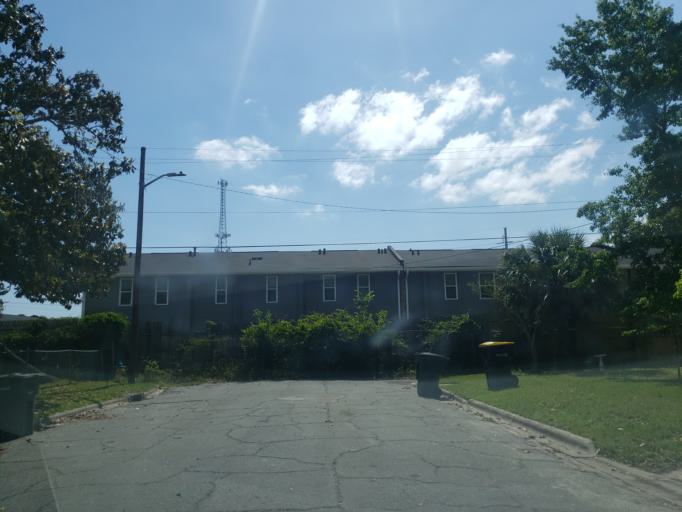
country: US
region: Georgia
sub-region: Chatham County
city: Thunderbolt
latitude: 32.0640
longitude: -81.0522
